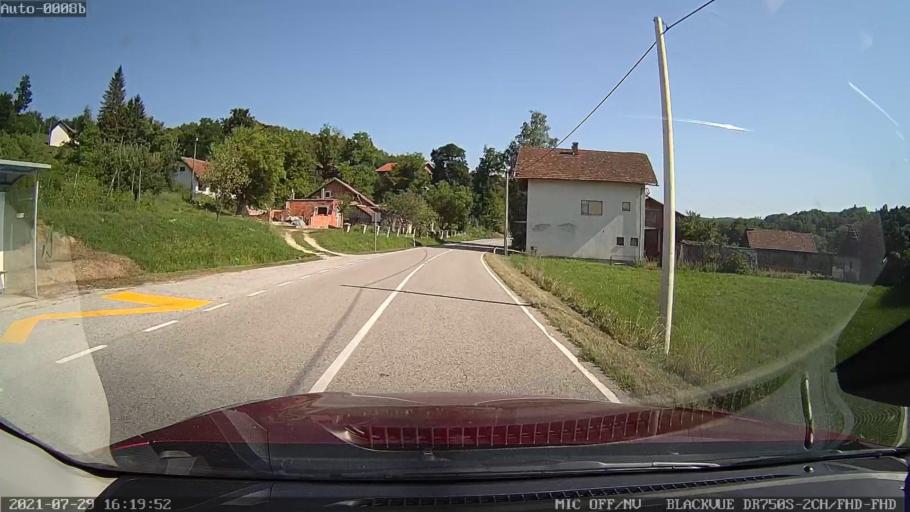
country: HR
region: Varazdinska
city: Lepoglava
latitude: 46.2453
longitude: 15.9600
